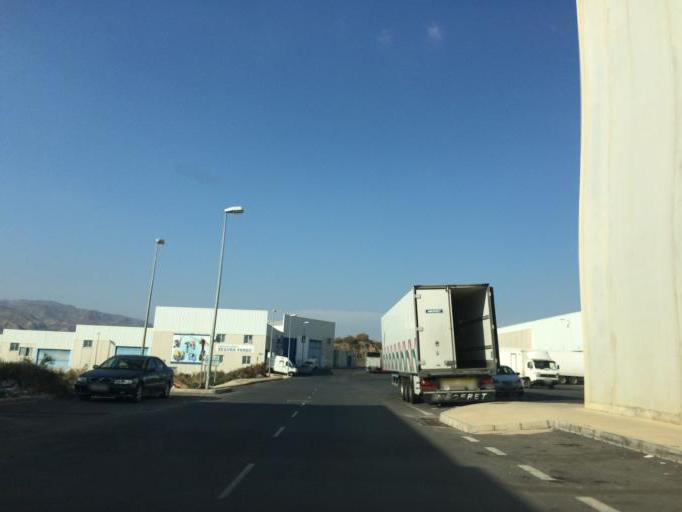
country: ES
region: Andalusia
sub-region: Provincia de Almeria
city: Viator
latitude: 36.8760
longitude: -2.4180
